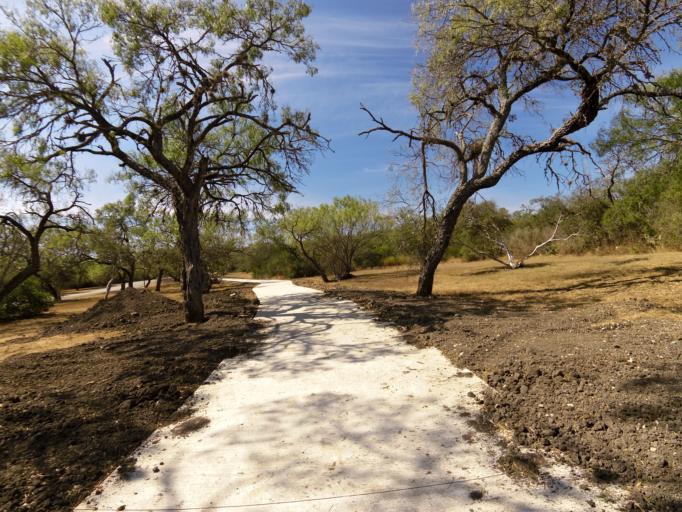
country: US
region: Texas
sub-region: Bexar County
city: San Antonio
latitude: 29.3851
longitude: -98.4314
